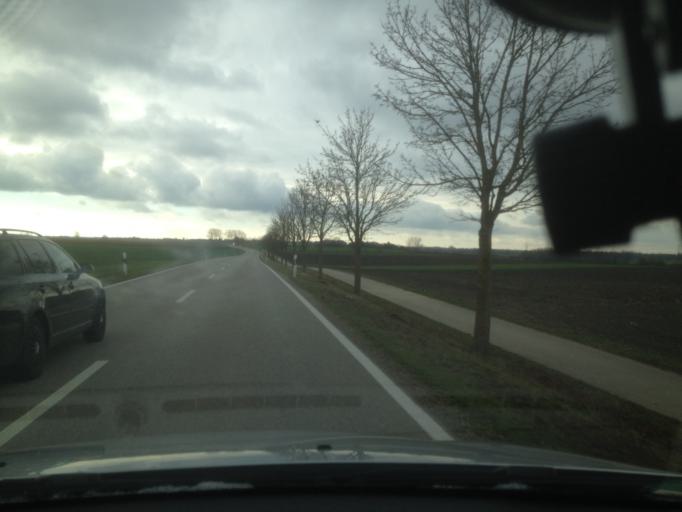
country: DE
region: Bavaria
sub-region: Swabia
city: Merching
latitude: 48.2546
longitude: 10.9729
